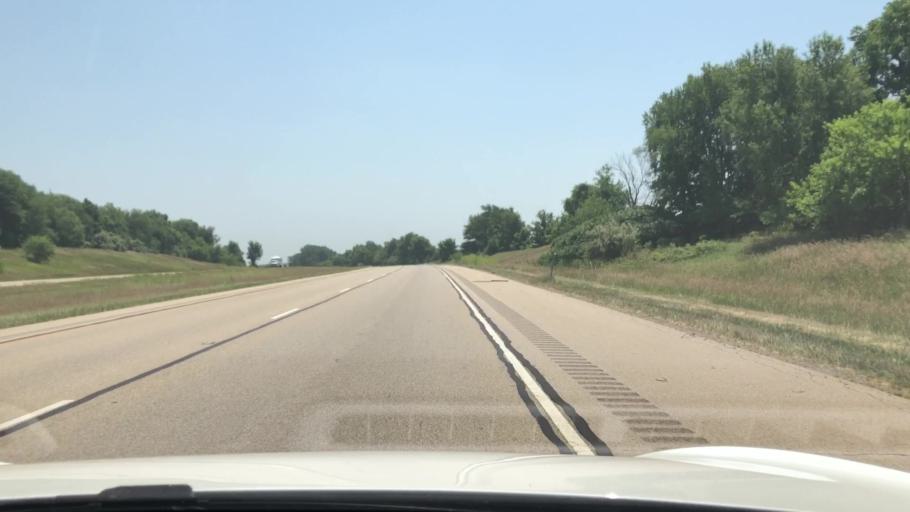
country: US
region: Illinois
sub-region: McLean County
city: Bloomington
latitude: 40.4261
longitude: -88.9529
